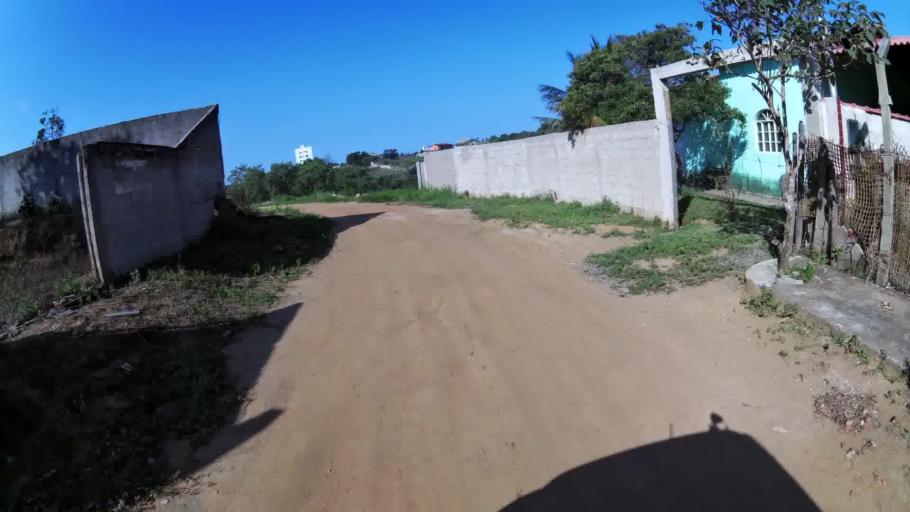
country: BR
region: Espirito Santo
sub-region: Guarapari
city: Guarapari
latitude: -20.7228
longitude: -40.5304
